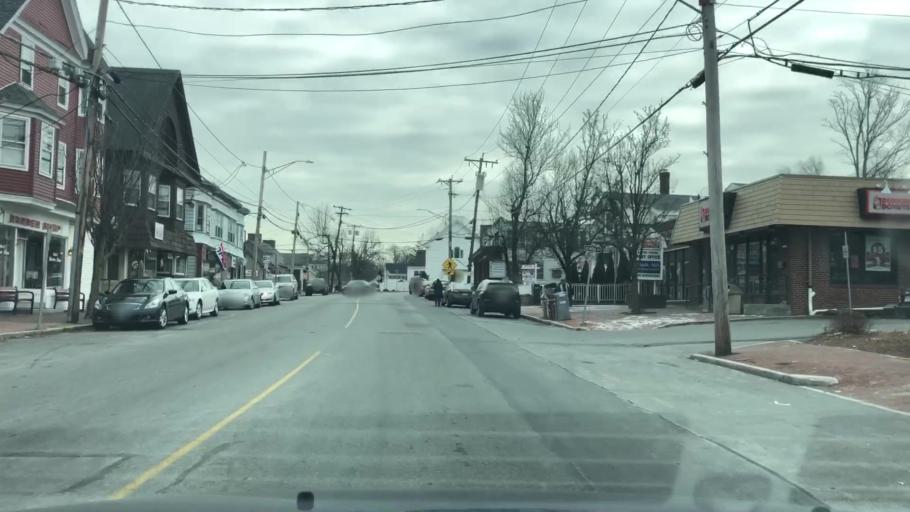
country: US
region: Massachusetts
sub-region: Essex County
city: North Andover
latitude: 42.7029
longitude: -71.1310
